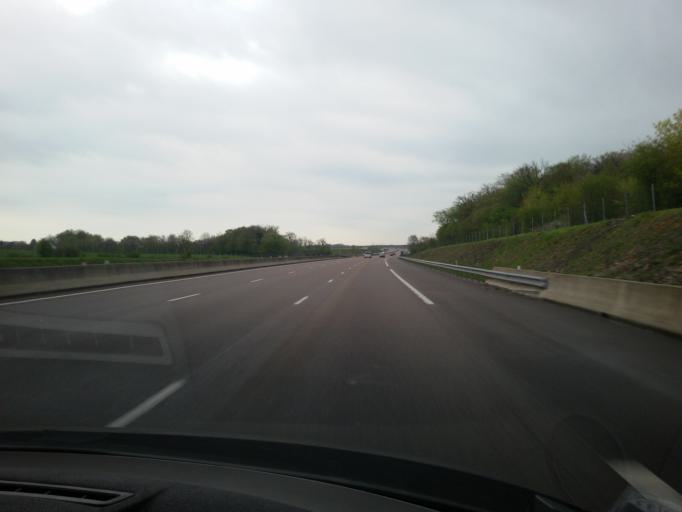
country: FR
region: Champagne-Ardenne
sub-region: Departement de la Haute-Marne
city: Langres
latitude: 47.8288
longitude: 5.2272
